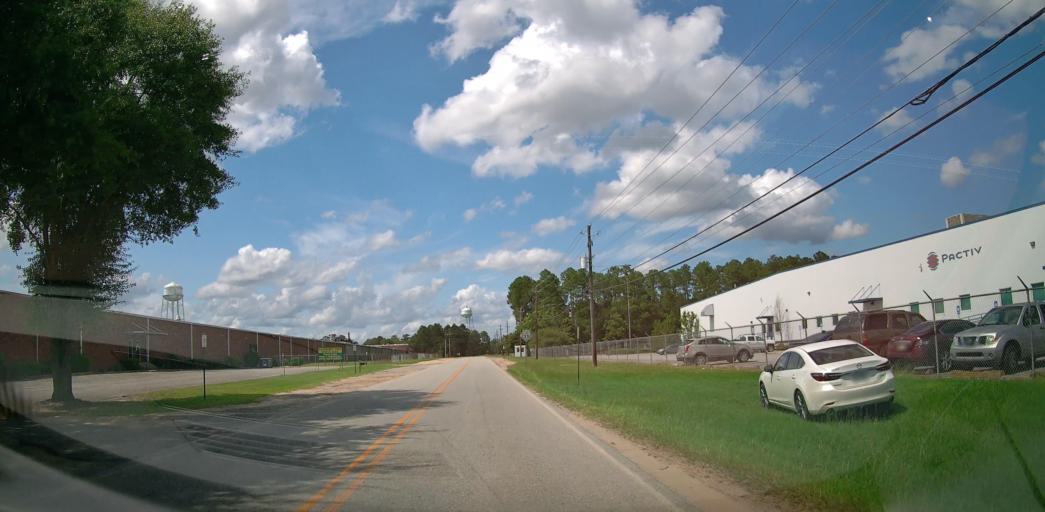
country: US
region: Georgia
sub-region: Houston County
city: Centerville
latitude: 32.7052
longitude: -83.6499
